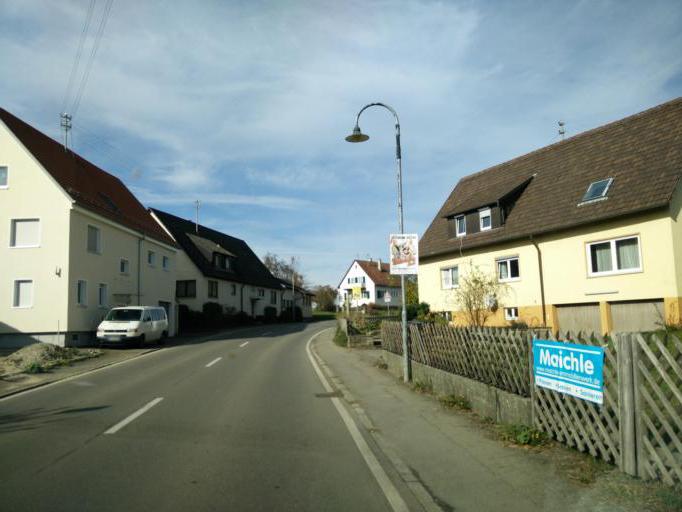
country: DE
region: Baden-Wuerttemberg
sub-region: Tuebingen Region
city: Gomaringen
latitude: 48.4876
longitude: 9.1061
